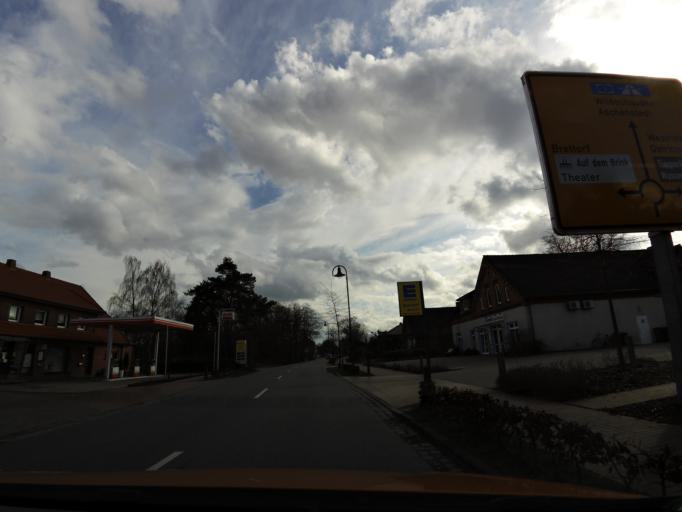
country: DE
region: Lower Saxony
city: Dotlingen
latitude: 52.9762
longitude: 8.3976
